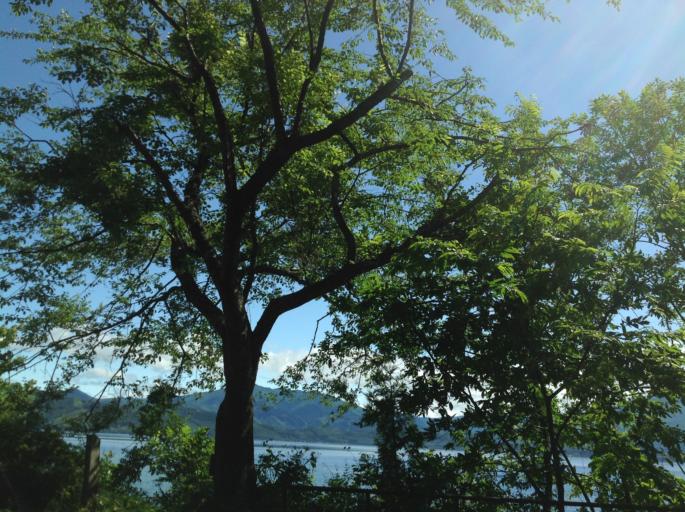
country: JP
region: Akita
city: Kakunodatemachi
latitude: 39.7112
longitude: 140.6346
